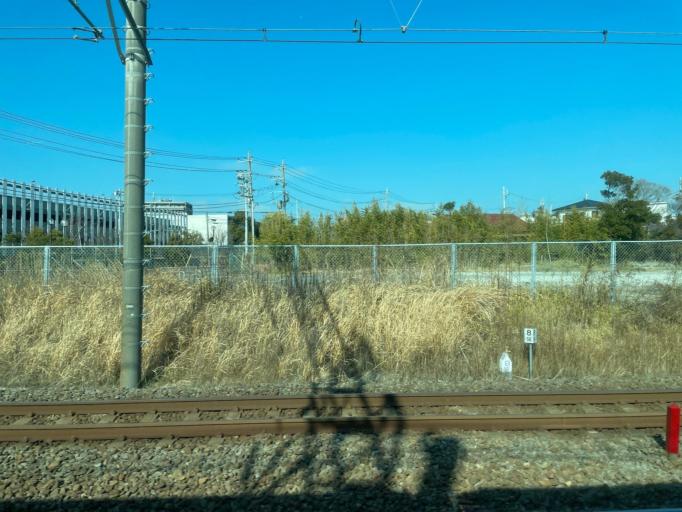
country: JP
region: Kanagawa
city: Chigasaki
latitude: 35.3360
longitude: 139.4245
